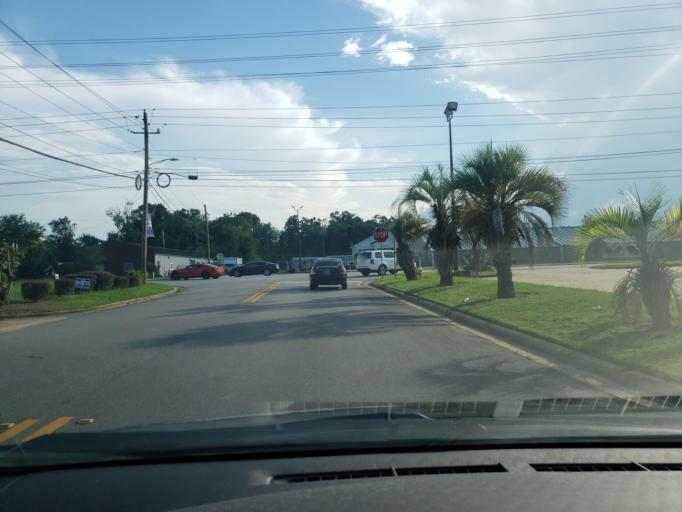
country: US
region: Georgia
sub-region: Dougherty County
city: Albany
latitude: 31.5847
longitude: -84.2046
